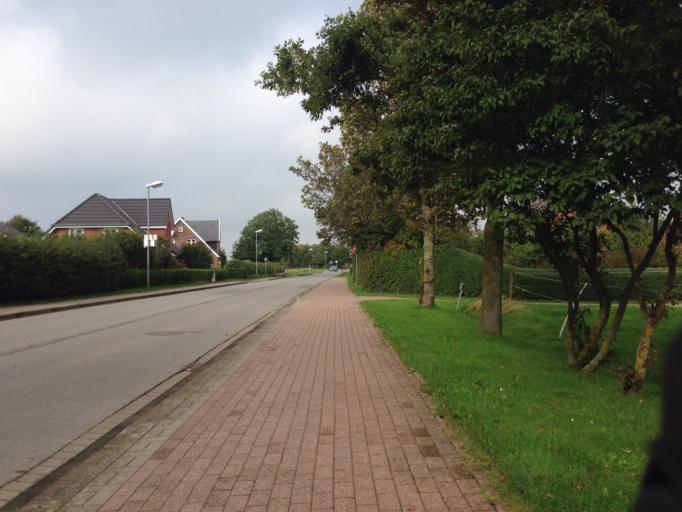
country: DE
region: Schleswig-Holstein
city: Wrixum
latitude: 54.7001
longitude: 8.5464
